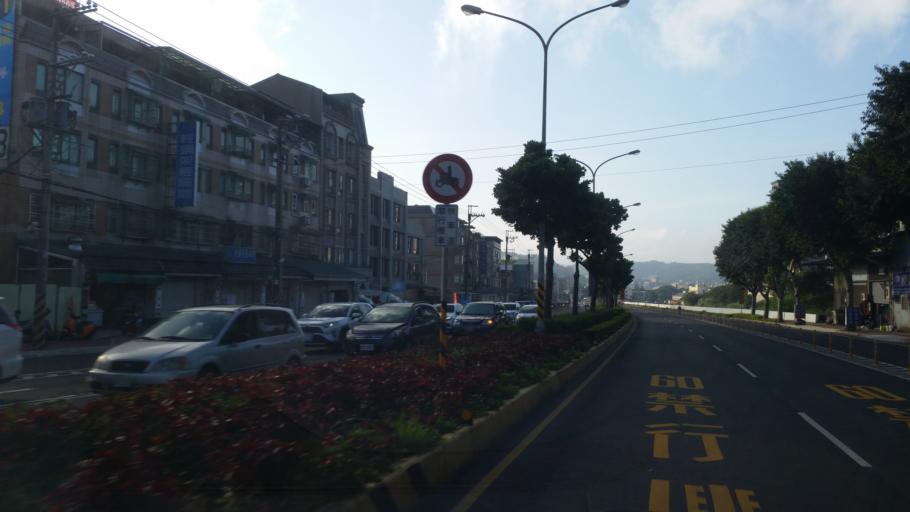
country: TW
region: Taiwan
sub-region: Taoyuan
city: Taoyuan
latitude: 25.0065
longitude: 121.3444
